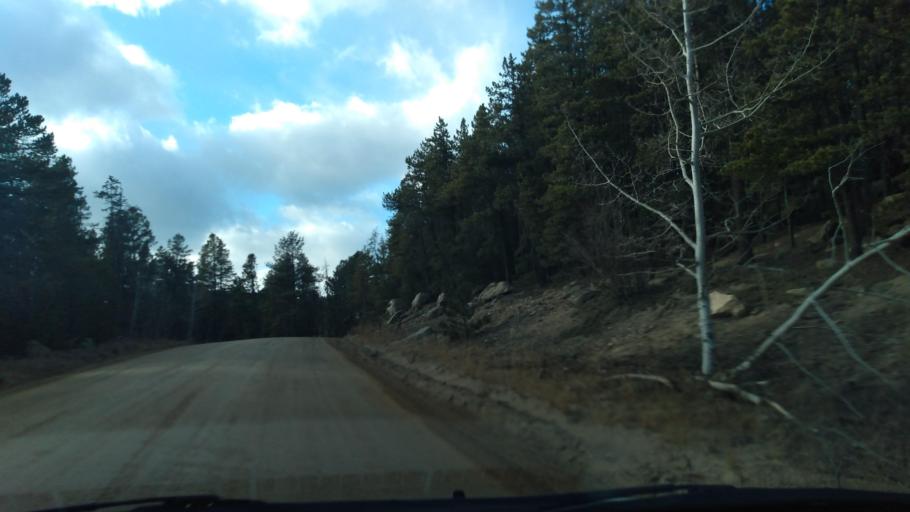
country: US
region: Colorado
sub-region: Boulder County
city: Nederland
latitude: 39.9508
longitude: -105.4512
